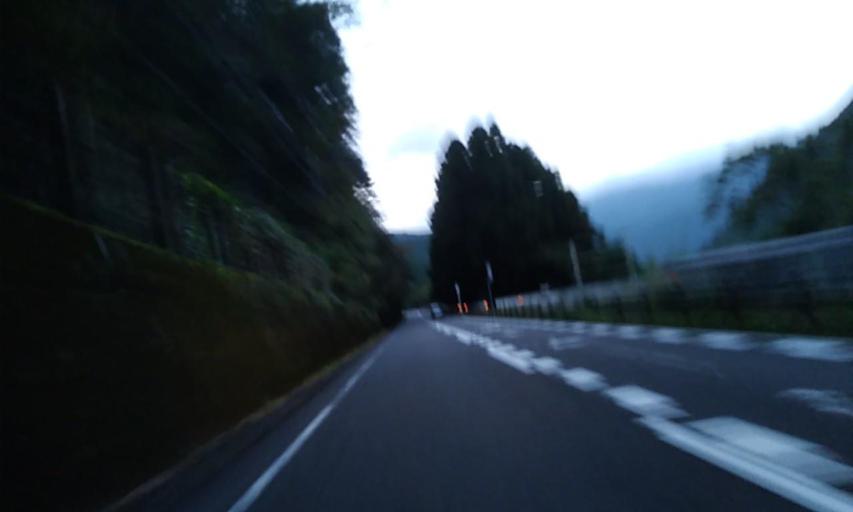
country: JP
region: Wakayama
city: Shingu
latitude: 33.7331
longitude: 135.9424
